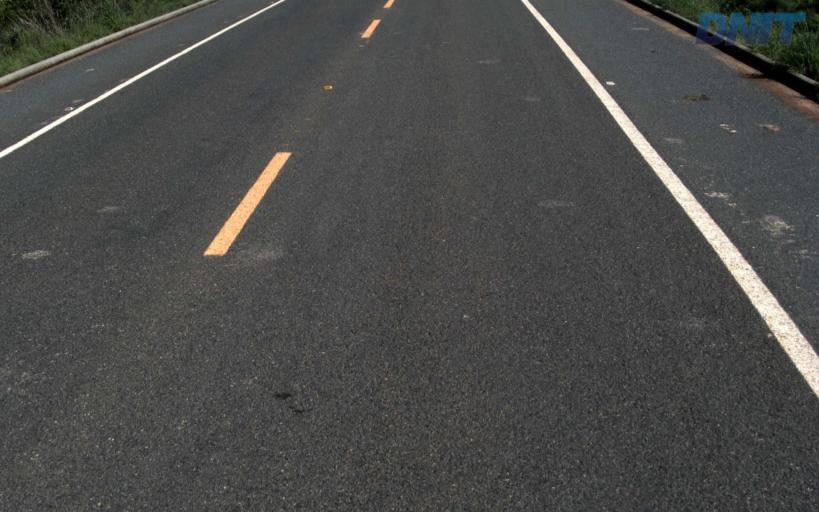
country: BR
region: Goias
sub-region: Sao Miguel Do Araguaia
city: Sao Miguel do Araguaia
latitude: -13.4138
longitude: -50.1312
